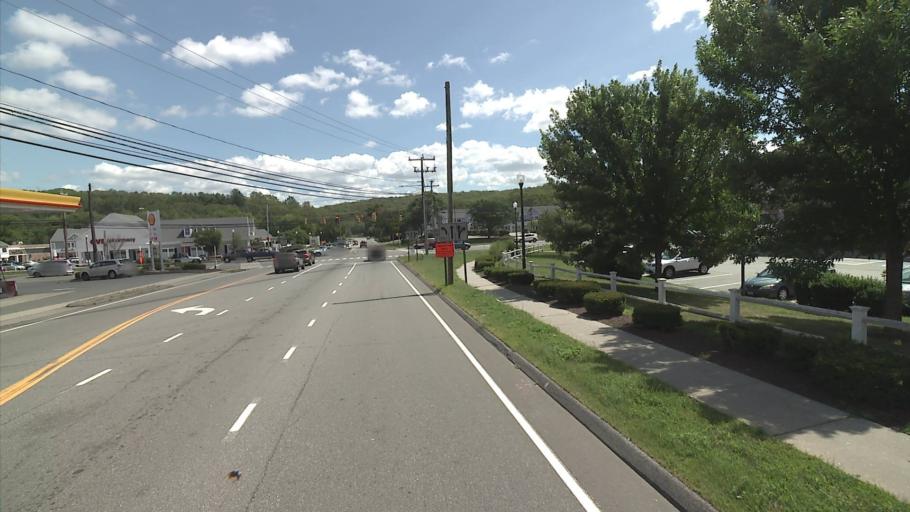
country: US
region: Connecticut
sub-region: New London County
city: Niantic
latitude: 41.3661
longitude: -72.2104
